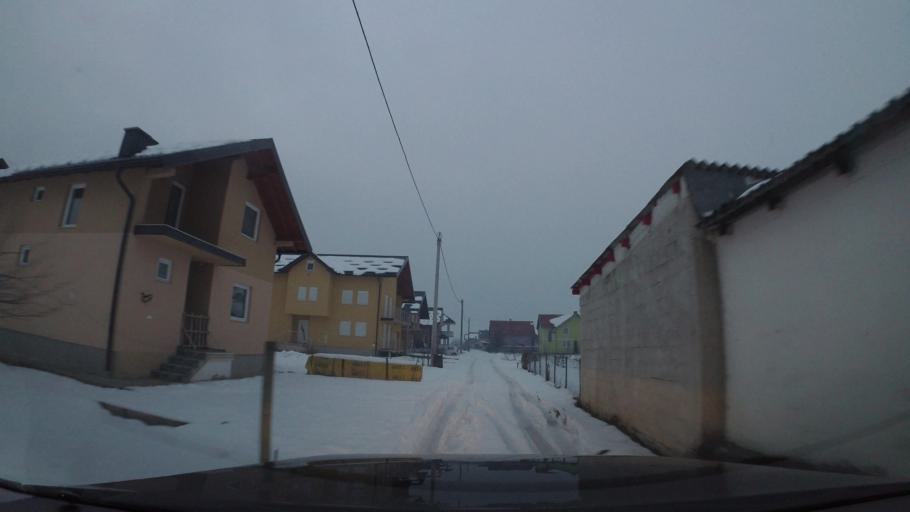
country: BA
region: Federation of Bosnia and Herzegovina
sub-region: Kanton Sarajevo
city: Sarajevo
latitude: 43.8548
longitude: 18.2911
